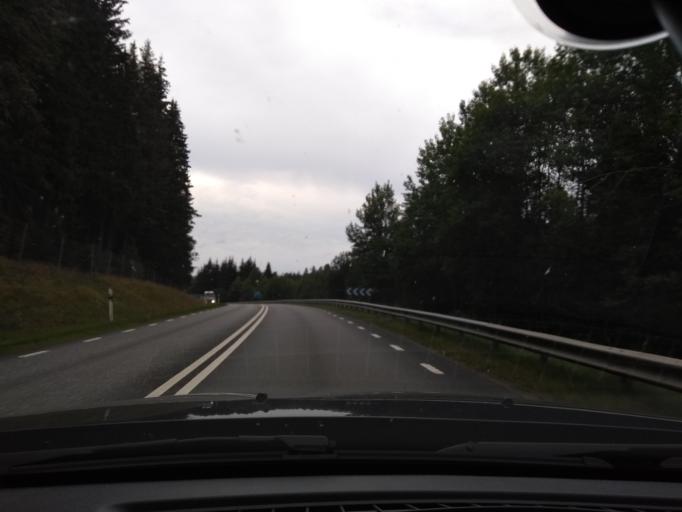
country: SE
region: Joenkoeping
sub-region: Eksjo Kommun
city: Eksjoe
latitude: 57.6397
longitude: 14.8441
